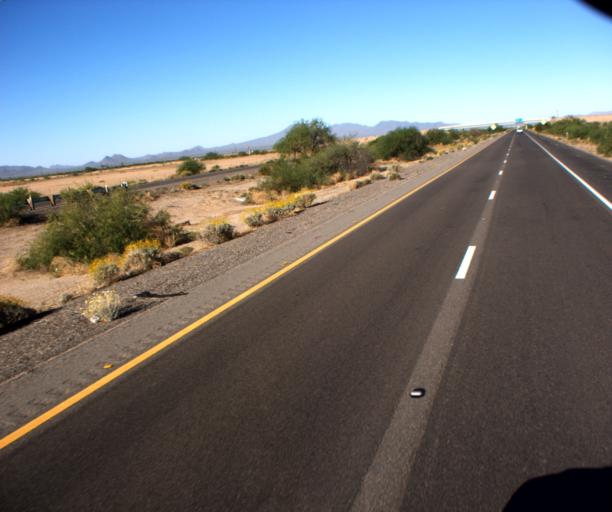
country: US
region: Arizona
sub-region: Pinal County
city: Casa Grande
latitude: 32.8282
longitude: -111.8724
